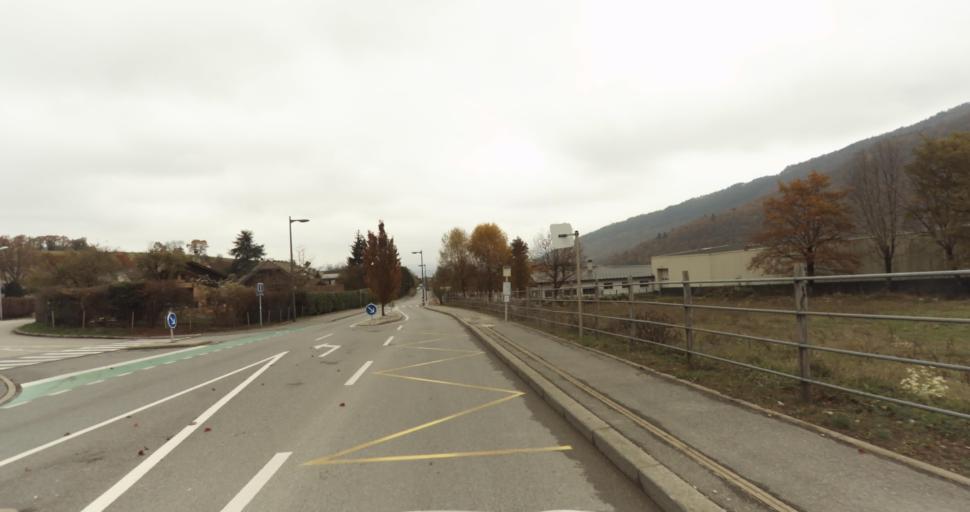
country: FR
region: Rhone-Alpes
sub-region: Departement de la Haute-Savoie
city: Seynod
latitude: 45.8715
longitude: 6.0993
